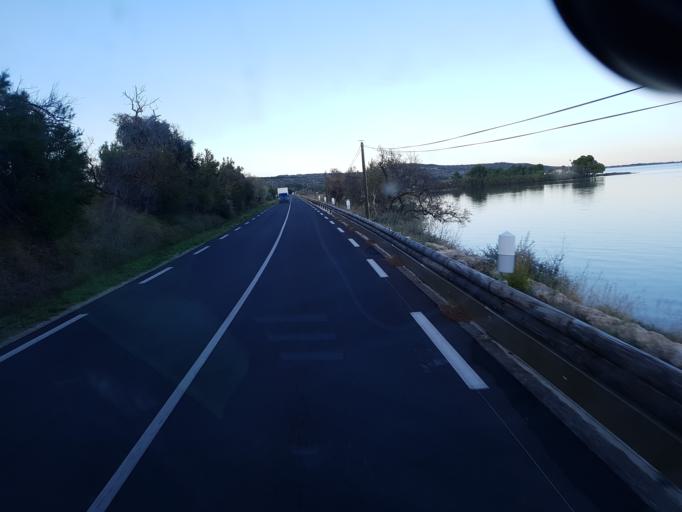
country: FR
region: Languedoc-Roussillon
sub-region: Departement de l'Aude
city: Leucate
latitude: 42.9650
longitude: 2.9968
